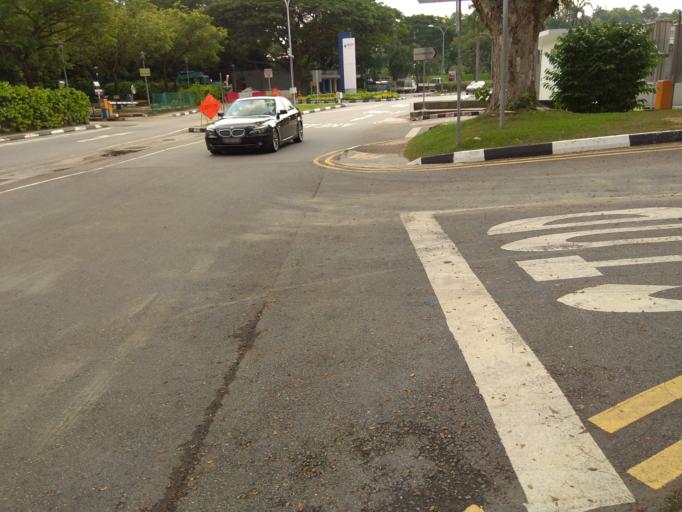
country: SG
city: Singapore
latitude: 1.2969
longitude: 103.7824
